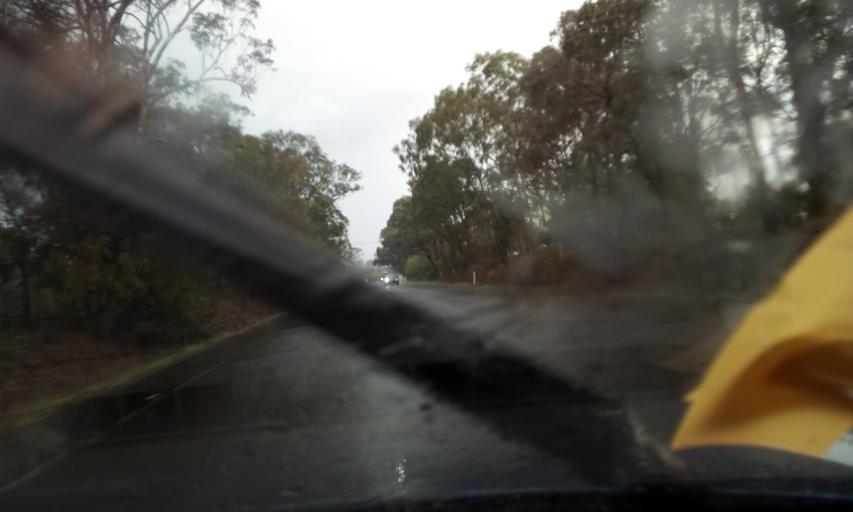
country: AU
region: New South Wales
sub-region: Wollondilly
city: Douglas Park
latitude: -34.2513
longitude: 150.7248
